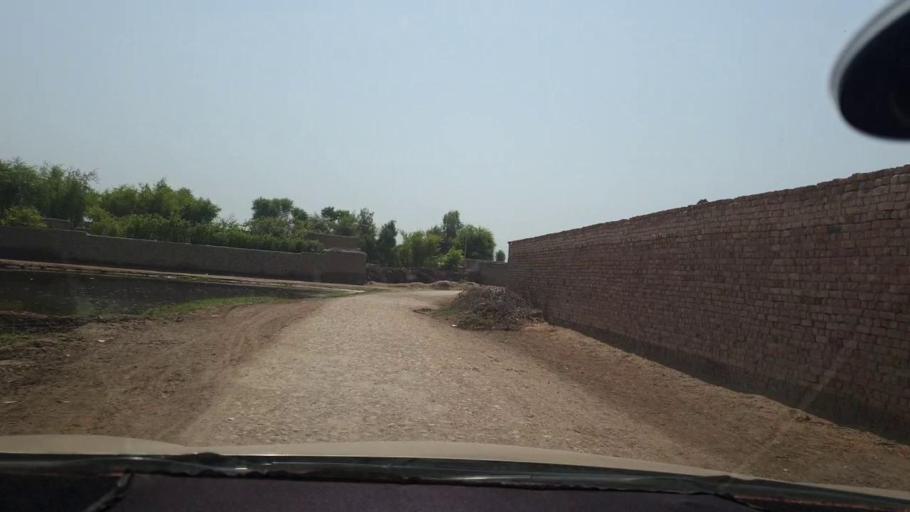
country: PK
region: Sindh
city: Kambar
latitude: 27.6346
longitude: 67.9330
